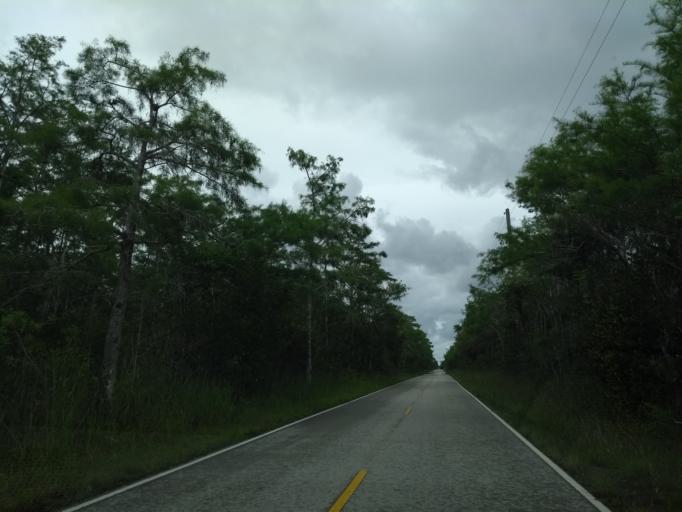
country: US
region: Florida
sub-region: Miami-Dade County
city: The Hammocks
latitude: 25.7613
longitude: -80.8960
